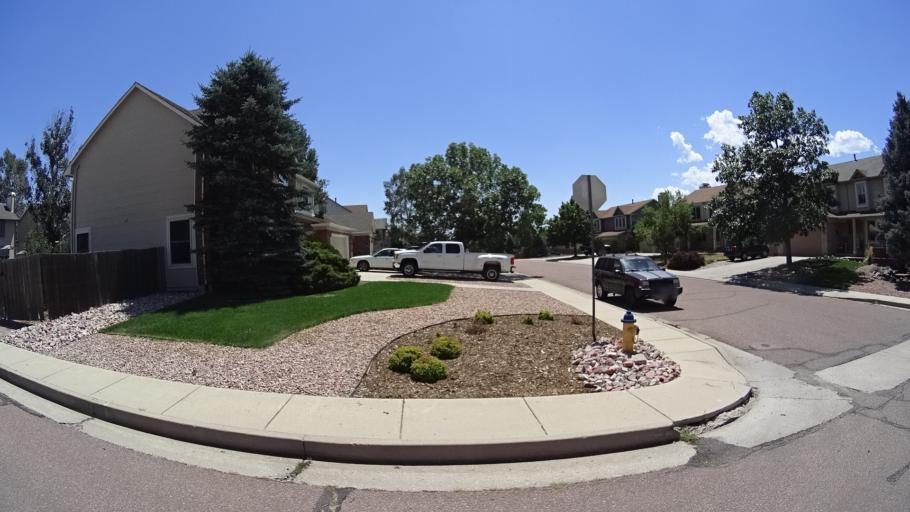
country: US
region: Colorado
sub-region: El Paso County
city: Black Forest
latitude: 38.9487
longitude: -104.7497
